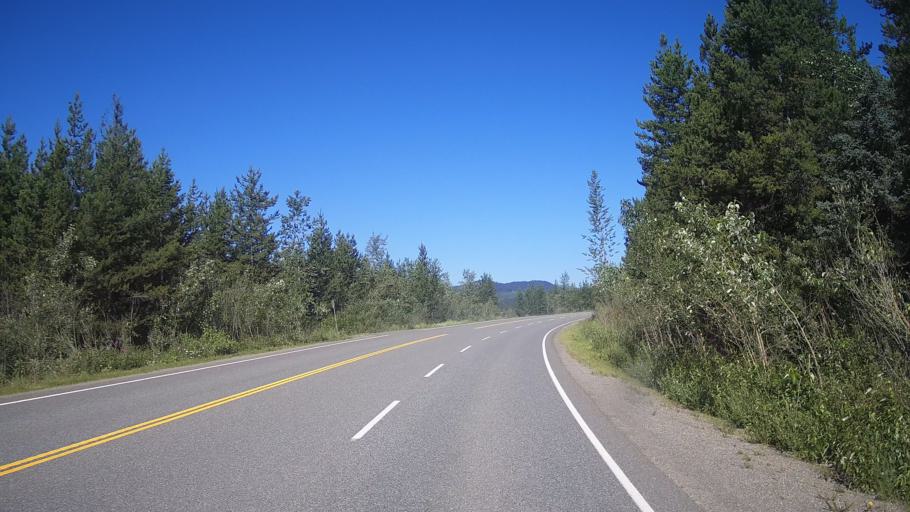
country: CA
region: British Columbia
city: Kamloops
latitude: 51.4944
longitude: -120.3344
